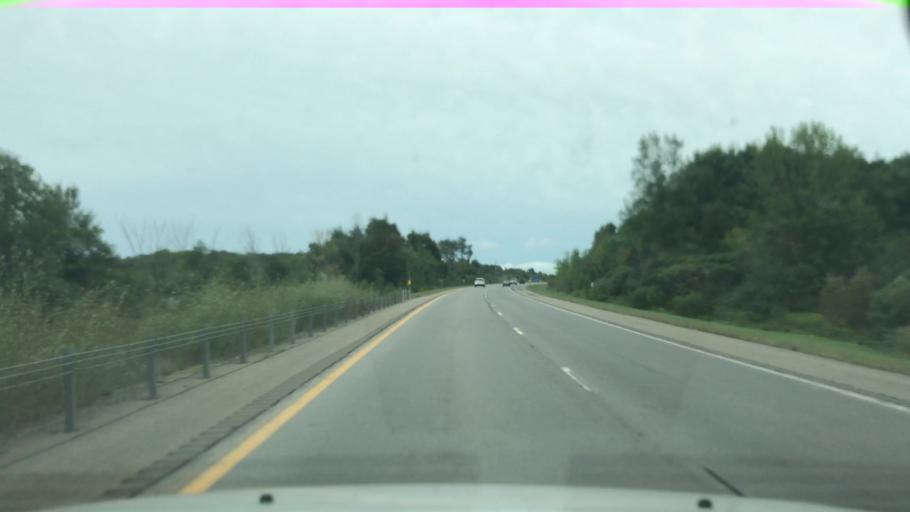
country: US
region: New York
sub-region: Erie County
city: Springville
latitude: 42.5681
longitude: -78.7138
